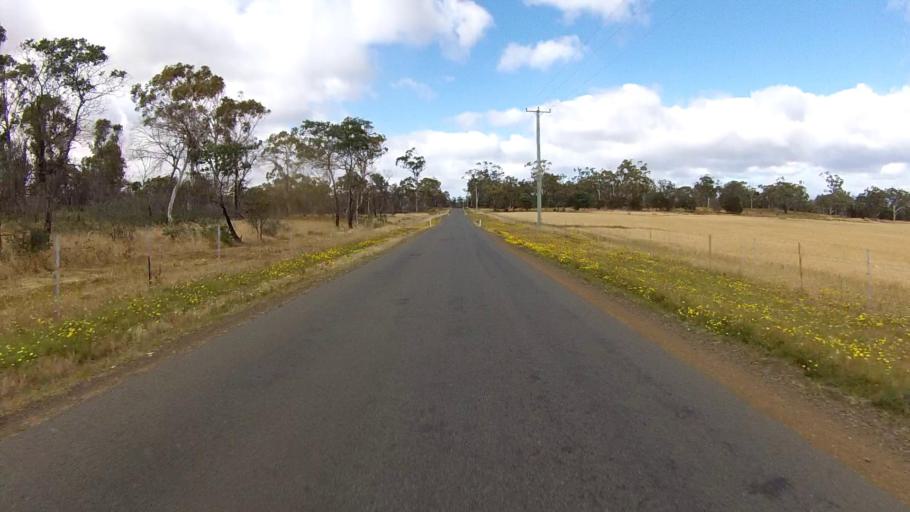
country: AU
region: Tasmania
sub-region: Northern Midlands
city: Evandale
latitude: -41.8128
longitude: 147.4255
